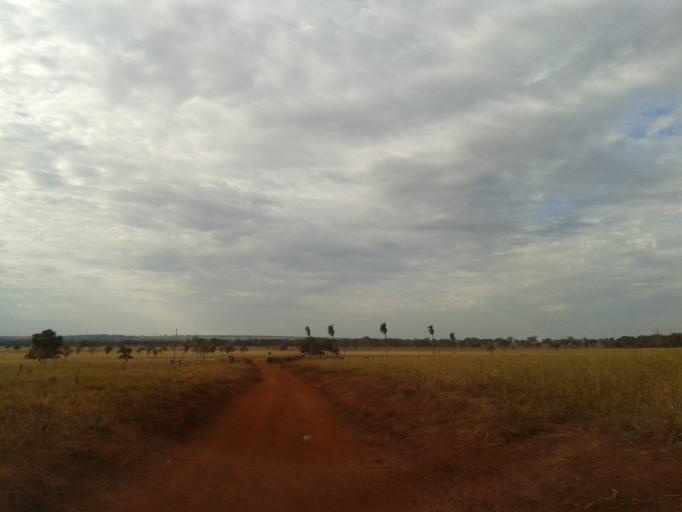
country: BR
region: Minas Gerais
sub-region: Santa Vitoria
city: Santa Vitoria
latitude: -18.7364
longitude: -50.2213
